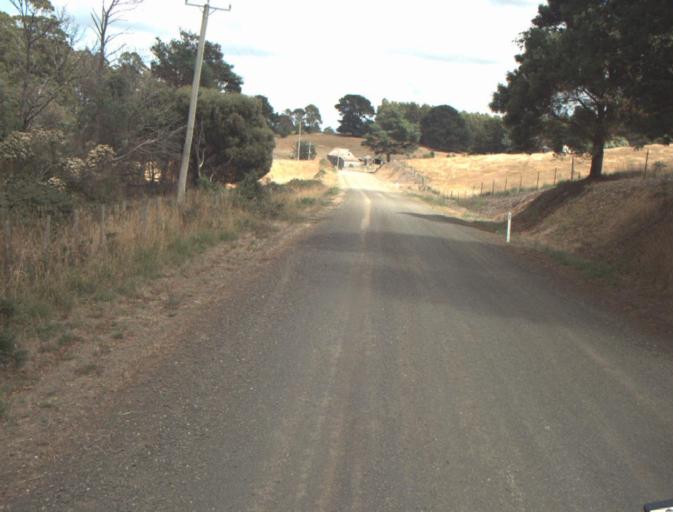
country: AU
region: Tasmania
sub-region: Launceston
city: Mayfield
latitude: -41.1918
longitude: 147.1885
